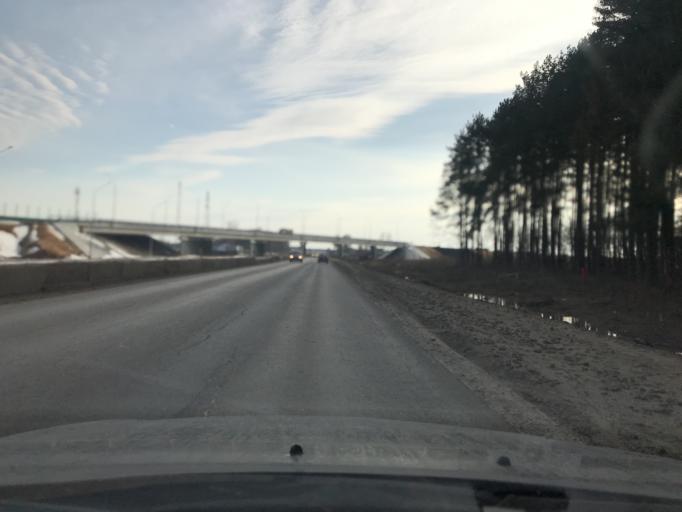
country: RU
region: Kaluga
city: Kaluga
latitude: 54.4433
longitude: 36.2291
